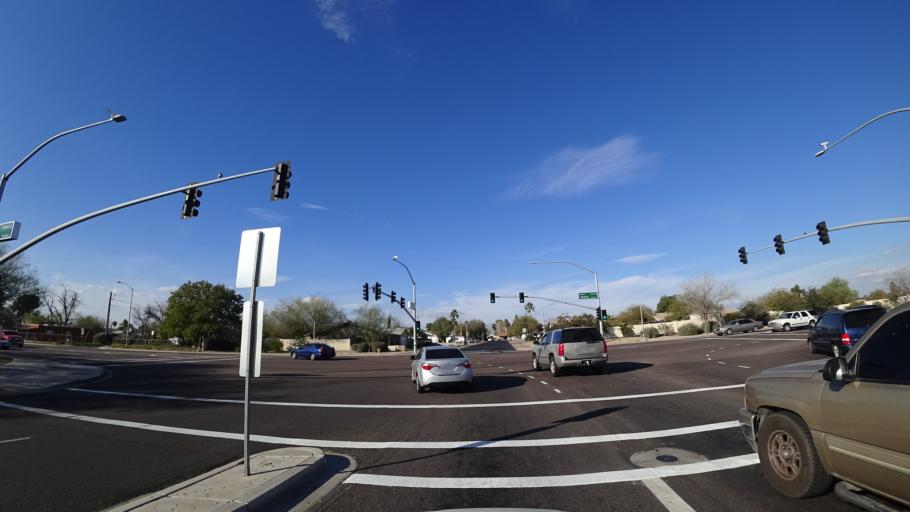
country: US
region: Arizona
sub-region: Maricopa County
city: Peoria
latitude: 33.5808
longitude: -112.2315
